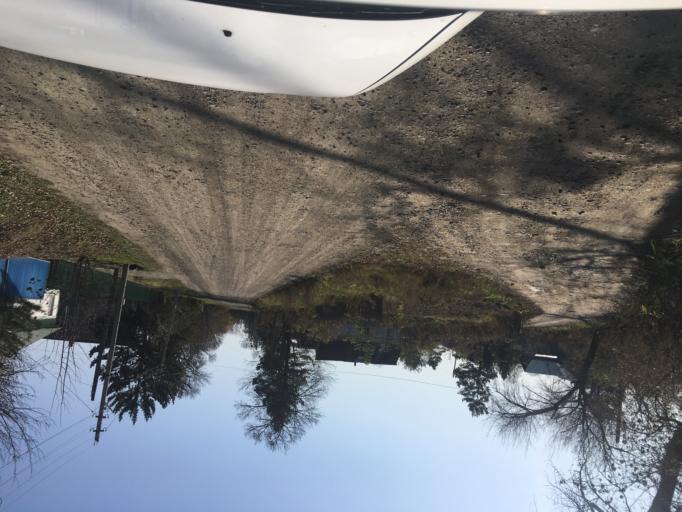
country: RU
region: Primorskiy
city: Dal'nerechensk
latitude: 45.9100
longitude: 133.7953
